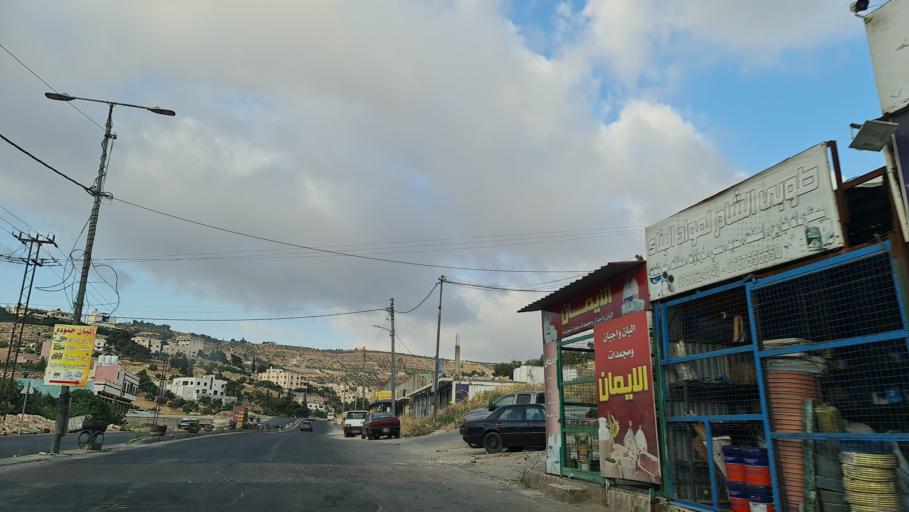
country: JO
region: Amman
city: Al Jubayhah
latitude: 32.0956
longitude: 35.9556
